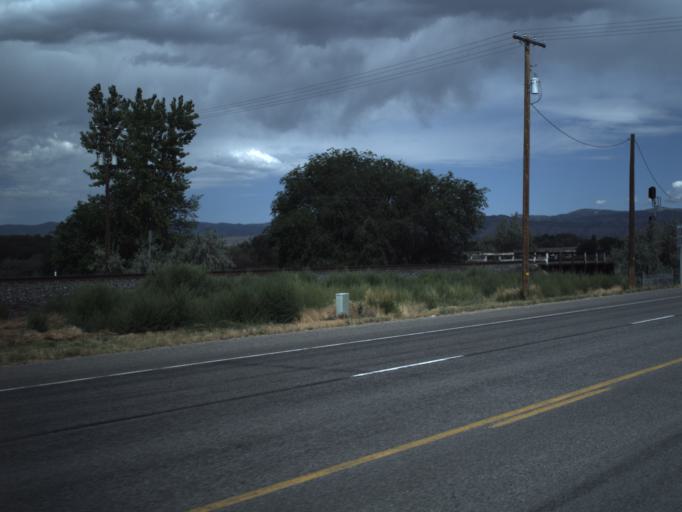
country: US
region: Utah
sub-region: Carbon County
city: Price
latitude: 39.5806
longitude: -110.7867
